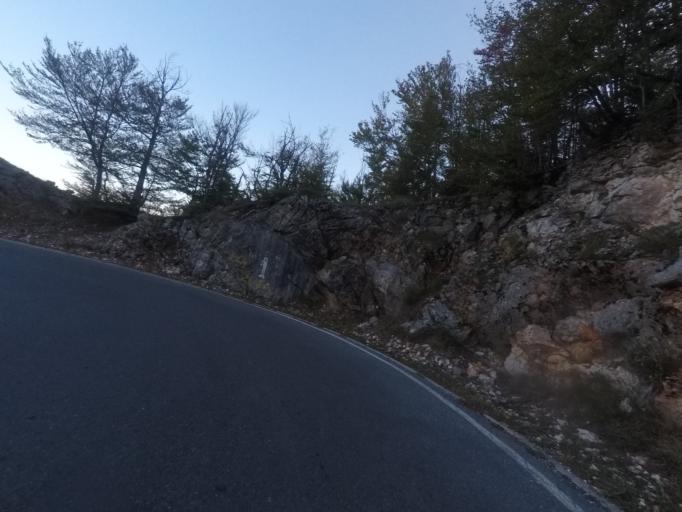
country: ME
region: Cetinje
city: Cetinje
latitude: 42.3832
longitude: 18.8540
